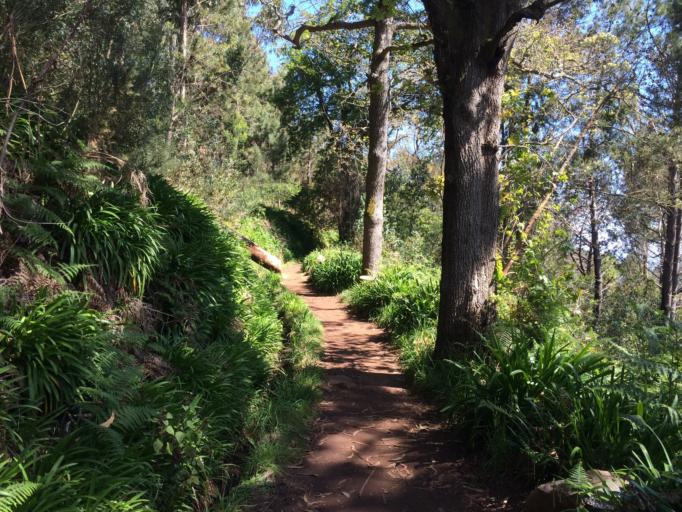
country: PT
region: Madeira
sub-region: Santa Cruz
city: Camacha
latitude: 32.6783
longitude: -16.8594
